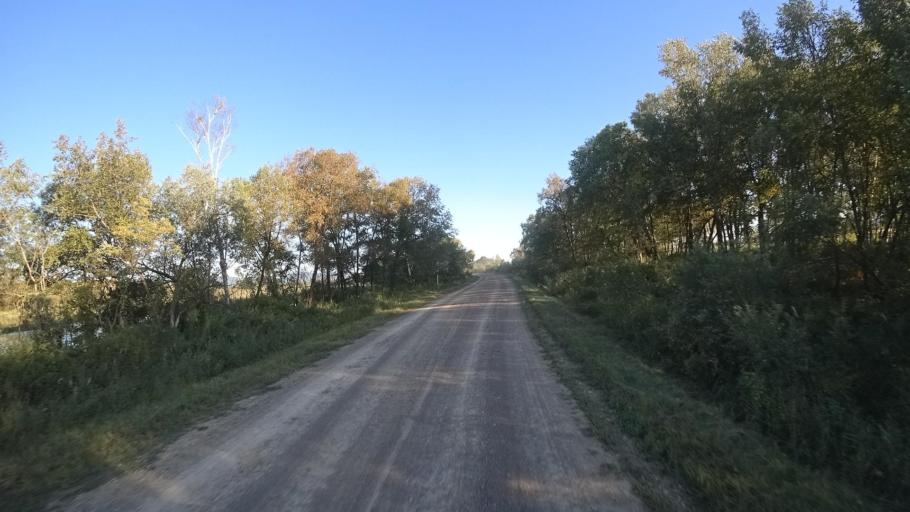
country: RU
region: Primorskiy
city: Kirovskiy
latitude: 44.8190
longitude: 133.6085
